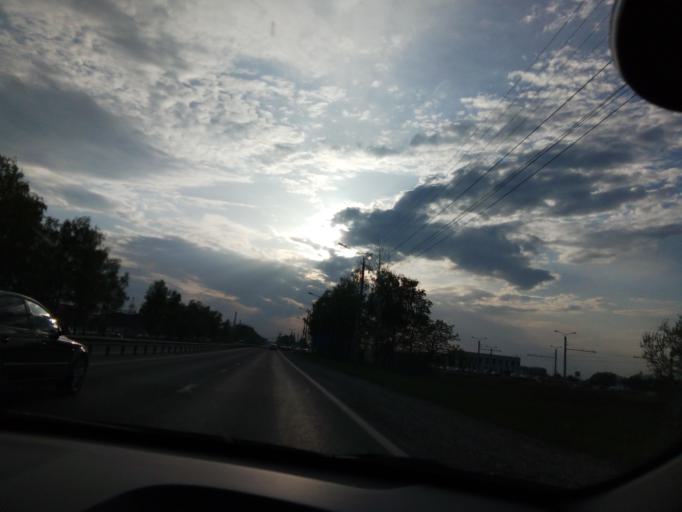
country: RU
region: Chuvashia
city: Novocheboksarsk
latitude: 56.1255
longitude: 47.3678
